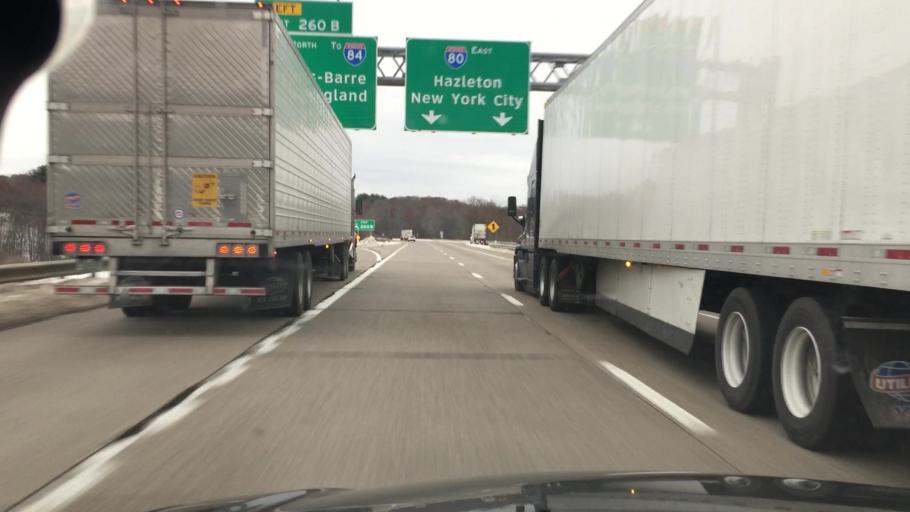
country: US
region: Pennsylvania
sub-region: Luzerne County
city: Conyngham
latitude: 41.0454
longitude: -76.0130
